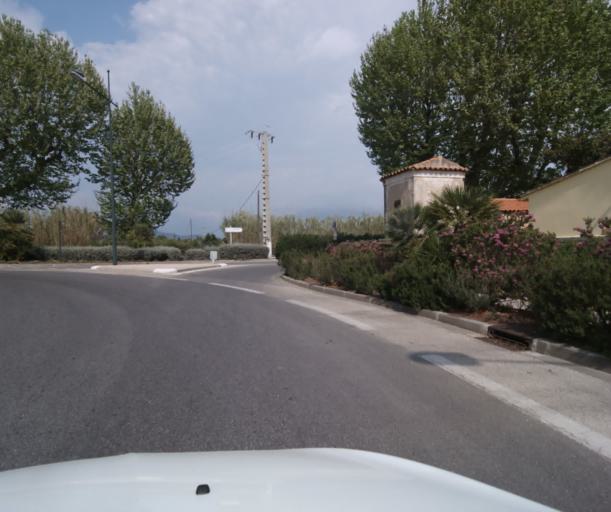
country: FR
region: Provence-Alpes-Cote d'Azur
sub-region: Departement du Var
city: Hyeres
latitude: 43.1062
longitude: 6.1424
